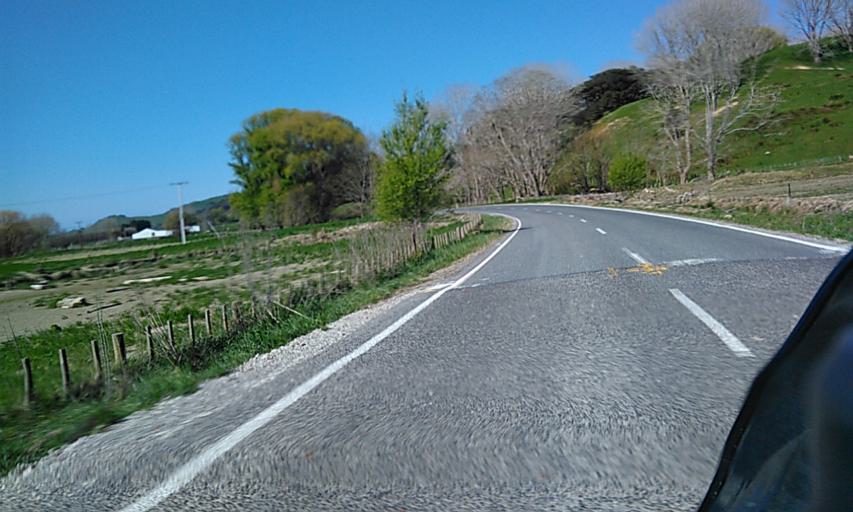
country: NZ
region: Gisborne
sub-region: Gisborne District
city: Gisborne
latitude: -38.3642
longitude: 178.2063
